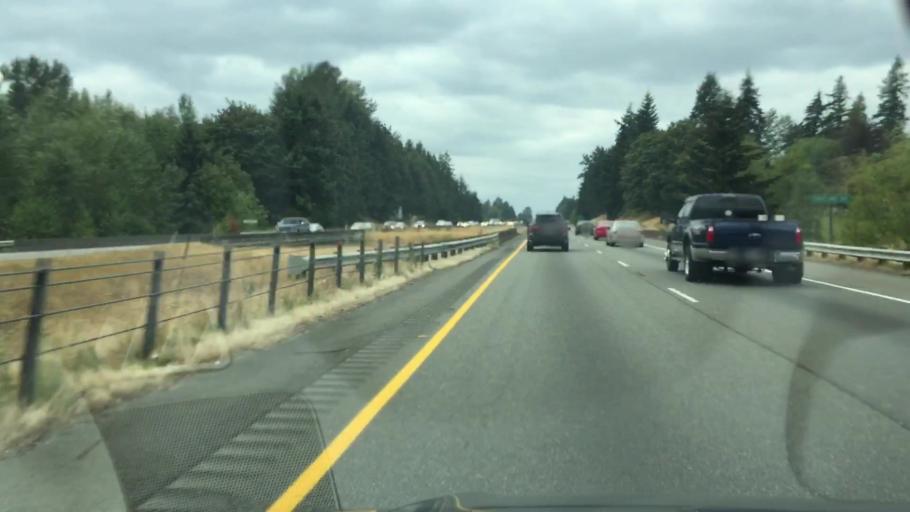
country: US
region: Washington
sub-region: Pierce County
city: Summit
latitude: 47.1584
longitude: -122.3274
